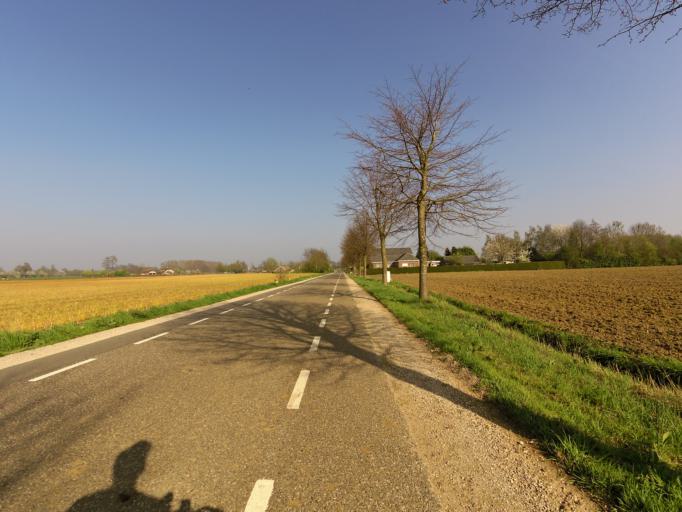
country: NL
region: Gelderland
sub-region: Gemeente Bronckhorst
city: Hengelo
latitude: 52.0344
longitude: 6.2682
